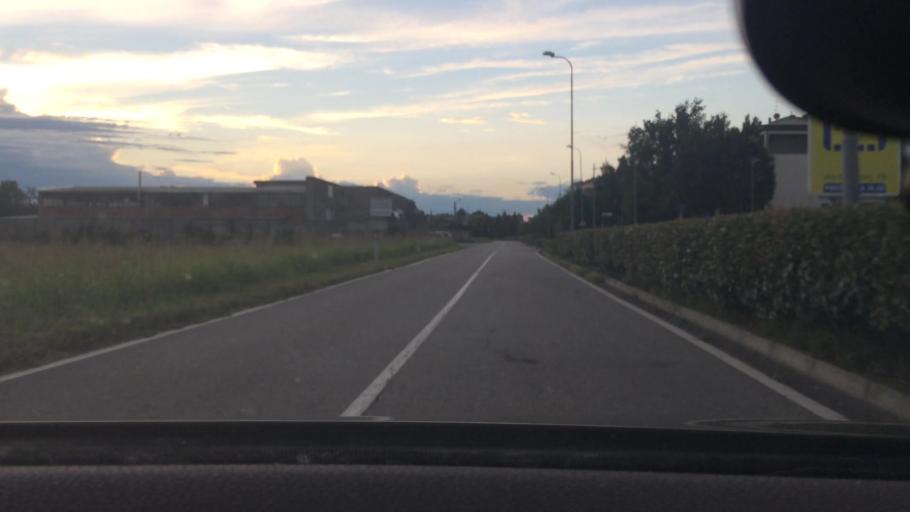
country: IT
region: Lombardy
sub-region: Citta metropolitana di Milano
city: Vanzago
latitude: 45.5212
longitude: 8.9962
